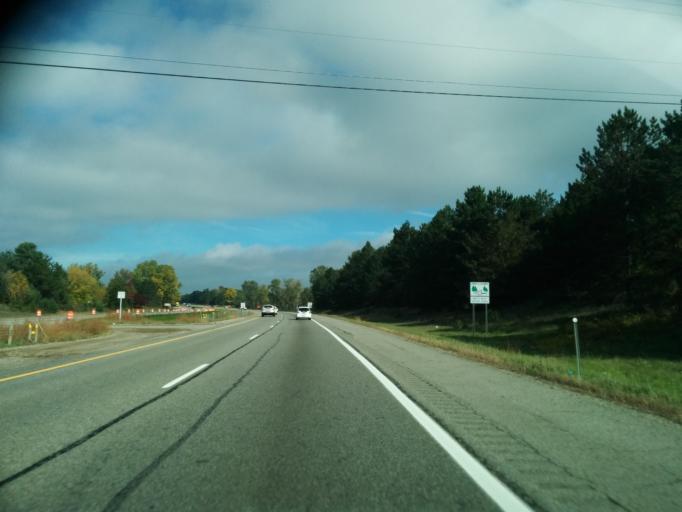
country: US
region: Michigan
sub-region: Livingston County
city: Brighton
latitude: 42.5378
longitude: -83.7497
